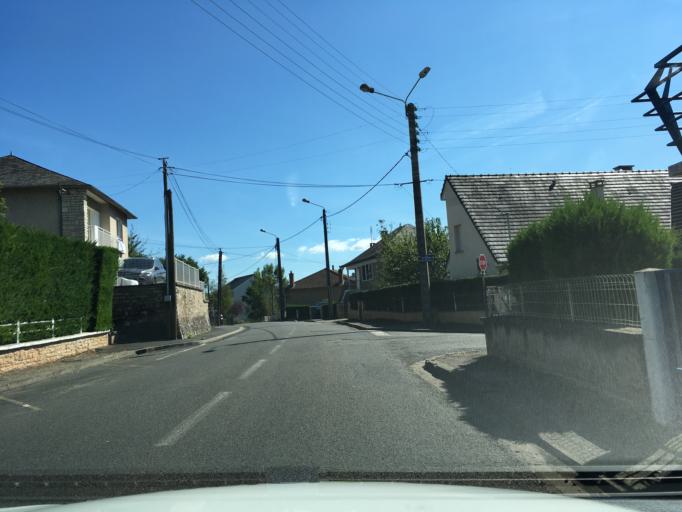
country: FR
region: Limousin
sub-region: Departement de la Correze
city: Ussac
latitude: 45.1669
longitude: 1.5120
